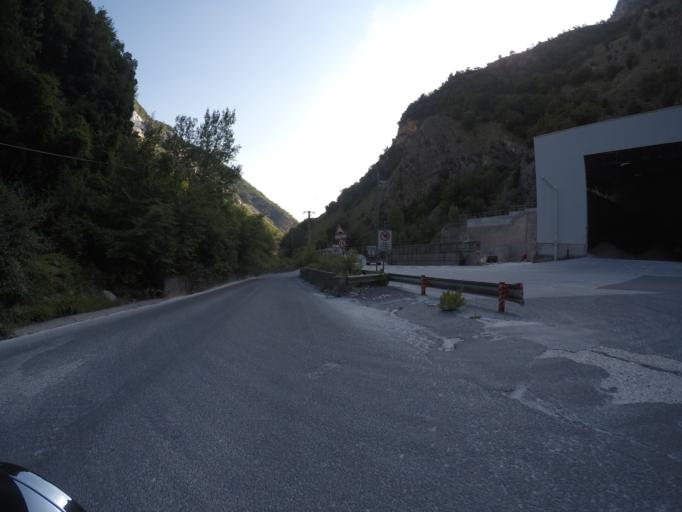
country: IT
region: Tuscany
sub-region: Provincia di Massa-Carrara
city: Carrara
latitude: 44.0990
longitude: 10.1198
